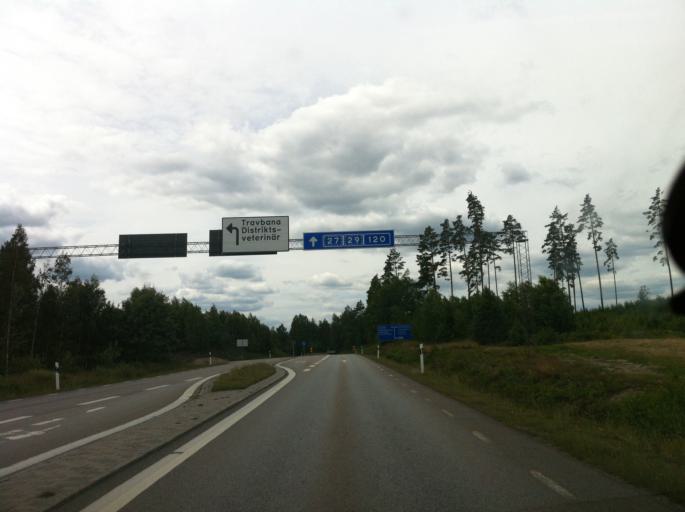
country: SE
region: Kronoberg
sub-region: Tingsryds Kommun
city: Tingsryd
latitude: 56.5143
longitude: 14.9964
